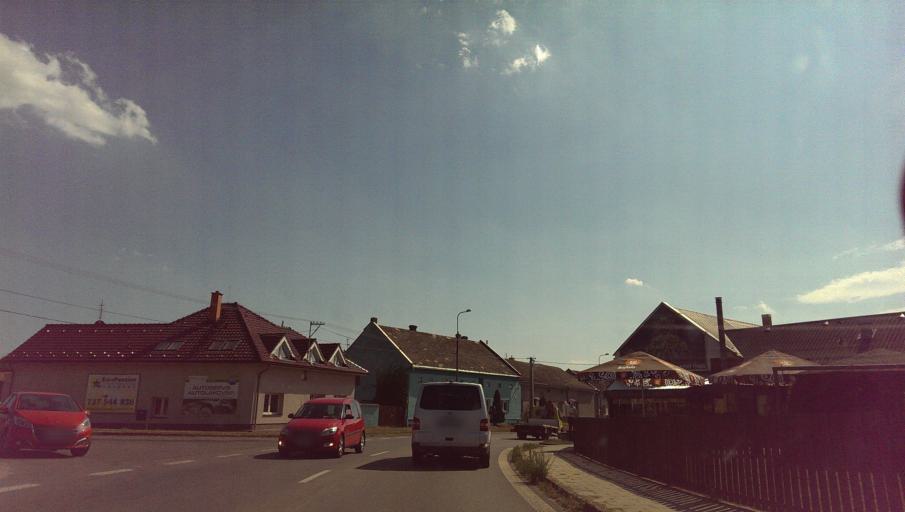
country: CZ
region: Zlin
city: Holesov
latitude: 49.3454
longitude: 17.6066
